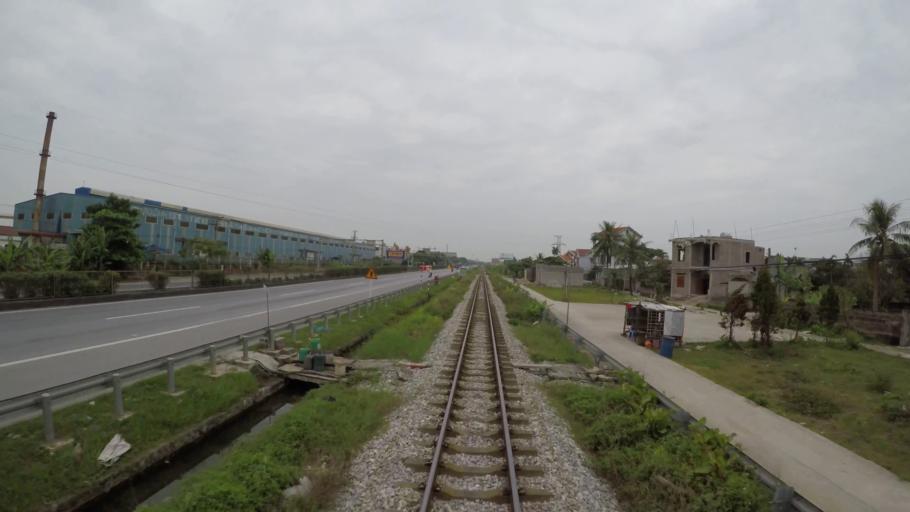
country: VN
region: Hai Duong
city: Phu Thai
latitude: 20.9465
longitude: 106.5389
